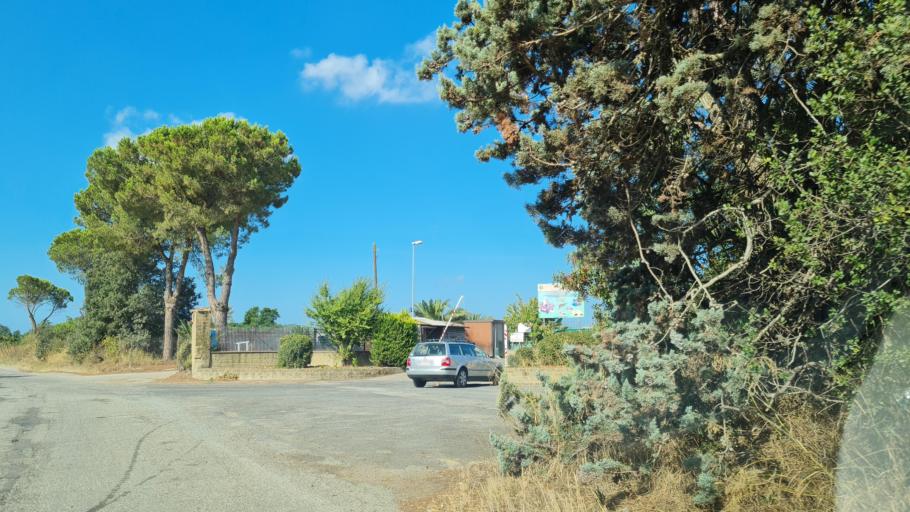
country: IT
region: Latium
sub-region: Provincia di Viterbo
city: Tarquinia
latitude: 42.2580
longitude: 11.7471
